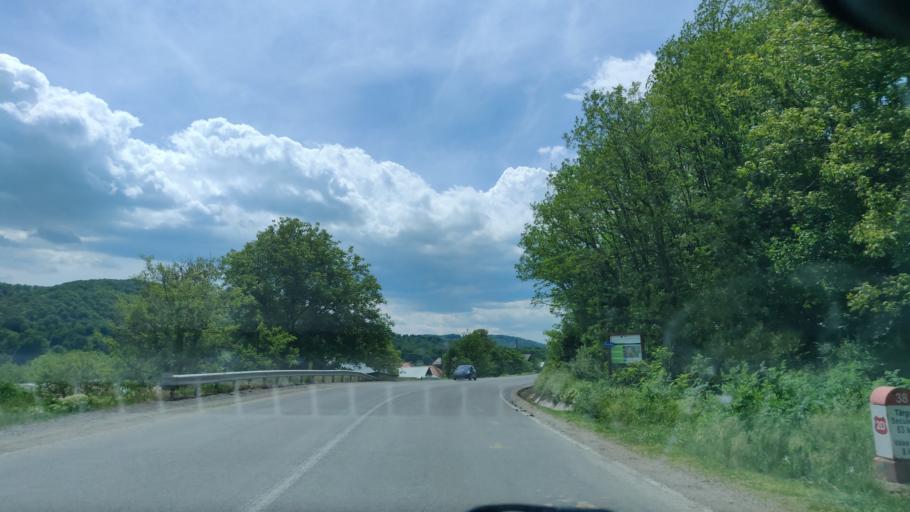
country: RO
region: Vrancea
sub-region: Comuna Vidra
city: Vidra
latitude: 45.8989
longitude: 26.8840
